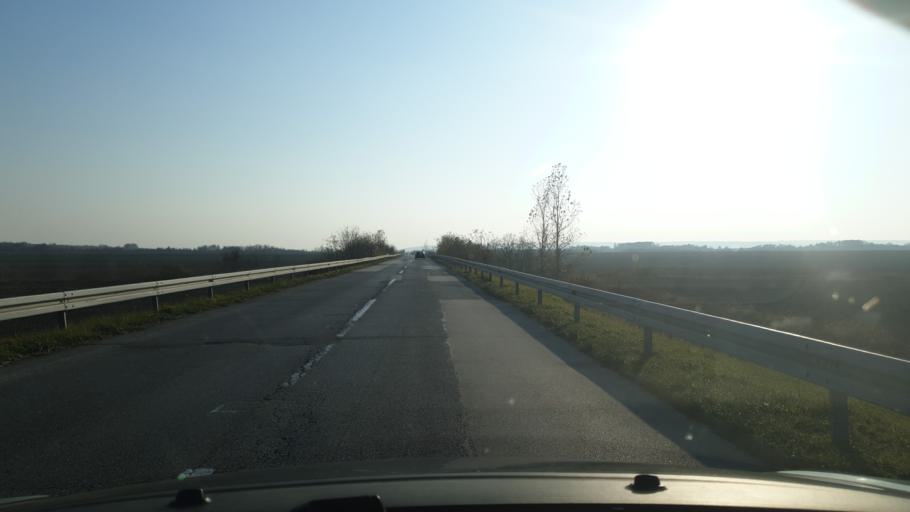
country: RS
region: Central Serbia
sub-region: Borski Okrug
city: Negotin
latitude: 44.1387
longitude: 22.3484
